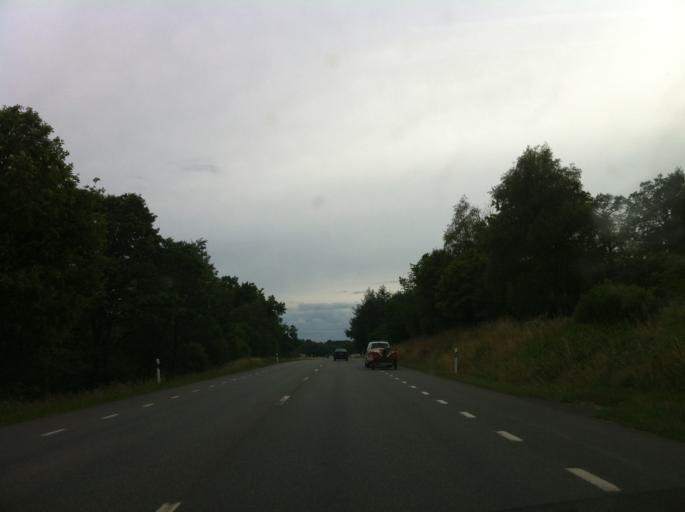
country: SE
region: Skane
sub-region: Hassleholms Kommun
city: Tormestorp
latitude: 56.0569
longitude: 13.7283
